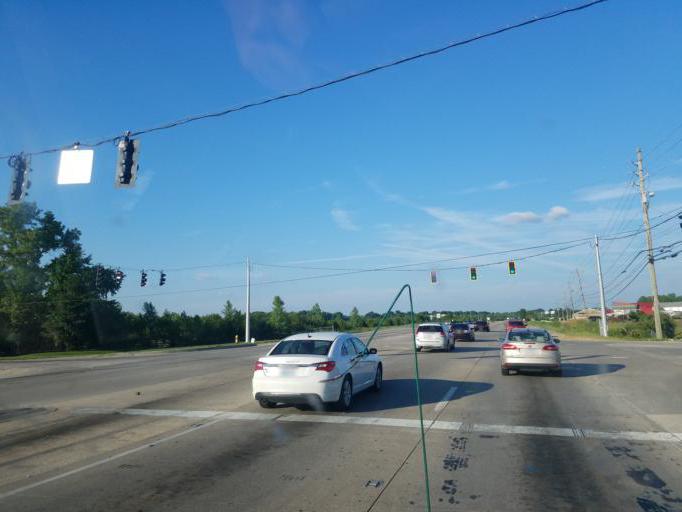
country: US
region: Kentucky
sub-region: Jefferson County
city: Heritage Creek
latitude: 38.1346
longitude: -85.7196
